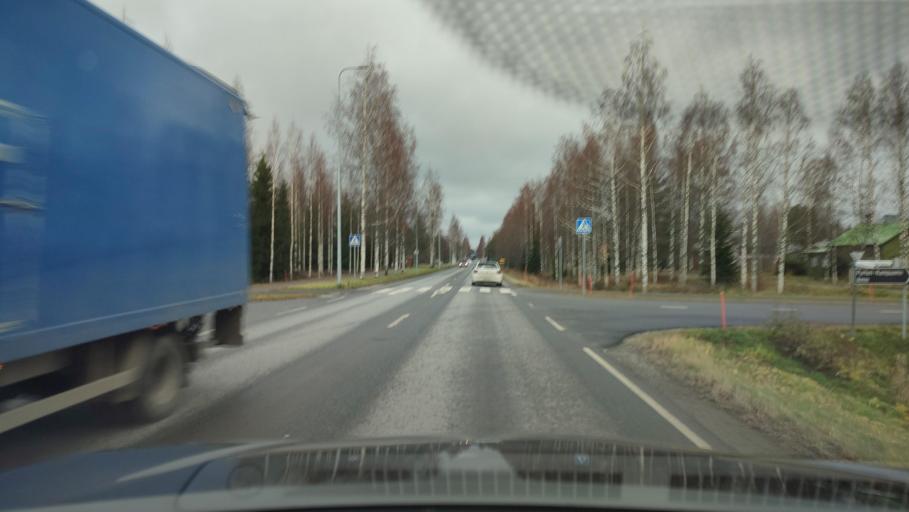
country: FI
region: Southern Ostrobothnia
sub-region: Suupohja
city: Kauhajoki
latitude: 62.4117
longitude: 22.1691
